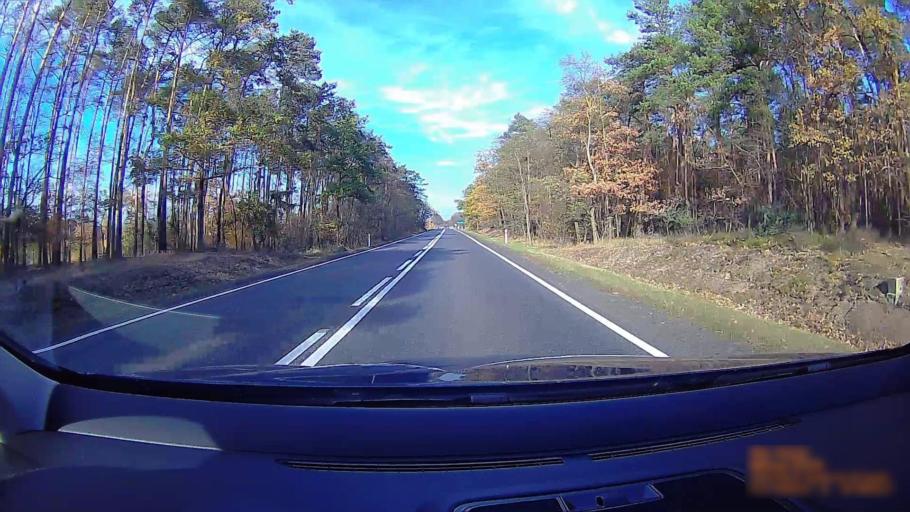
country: PL
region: Greater Poland Voivodeship
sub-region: Powiat koninski
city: Rychwal
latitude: 51.9948
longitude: 18.1419
